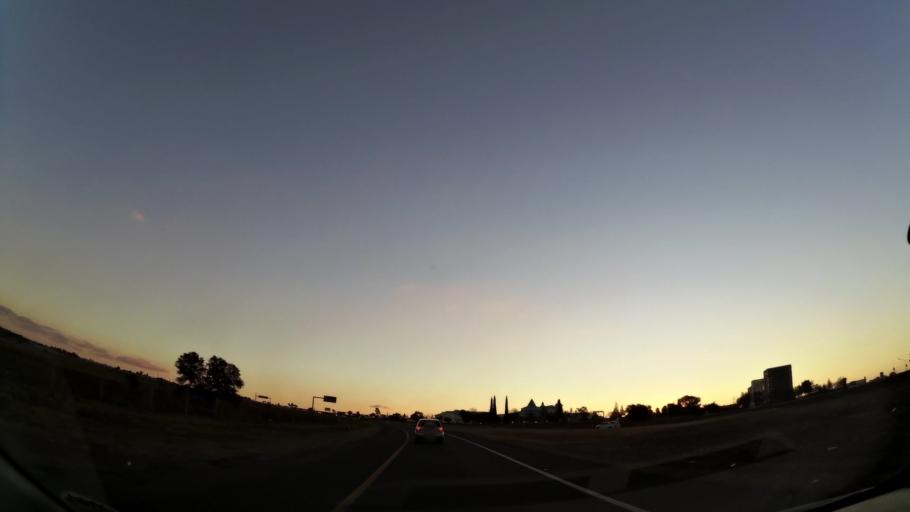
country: ZA
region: Mpumalanga
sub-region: Nkangala District Municipality
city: Witbank
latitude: -25.8887
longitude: 29.2712
